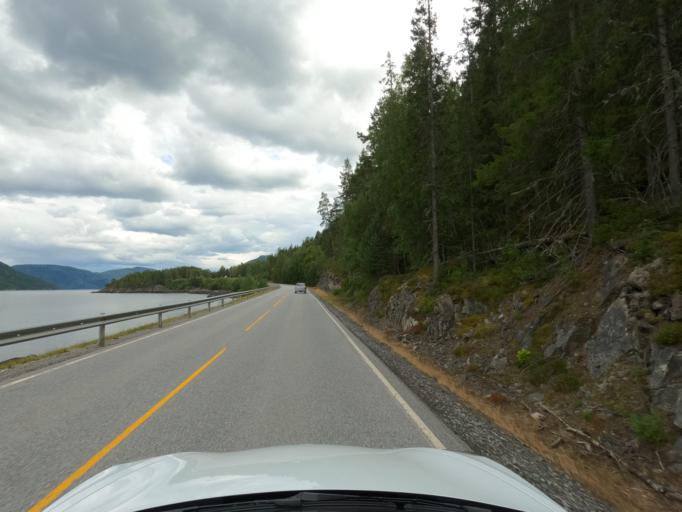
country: NO
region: Telemark
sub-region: Hjartdal
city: Sauland
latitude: 59.8654
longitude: 8.9341
